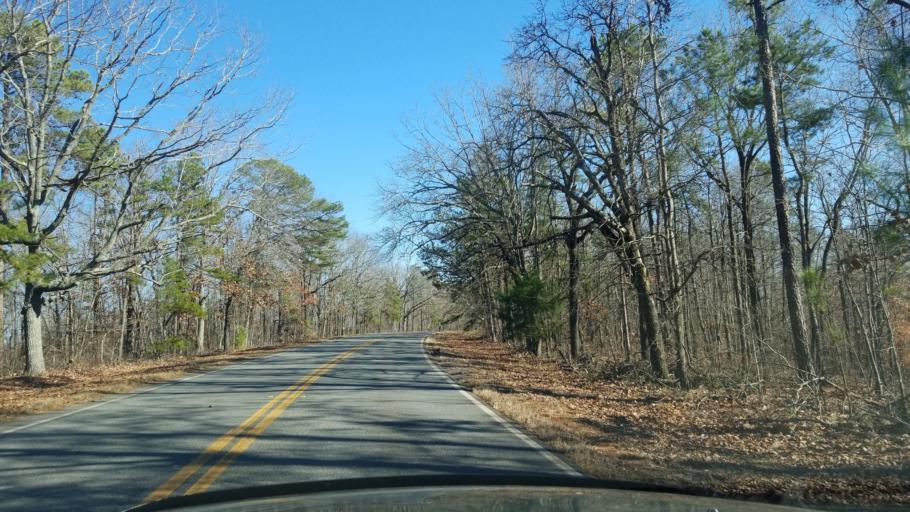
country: US
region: Georgia
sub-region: Talbot County
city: Sardis
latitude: 32.8437
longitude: -84.6883
